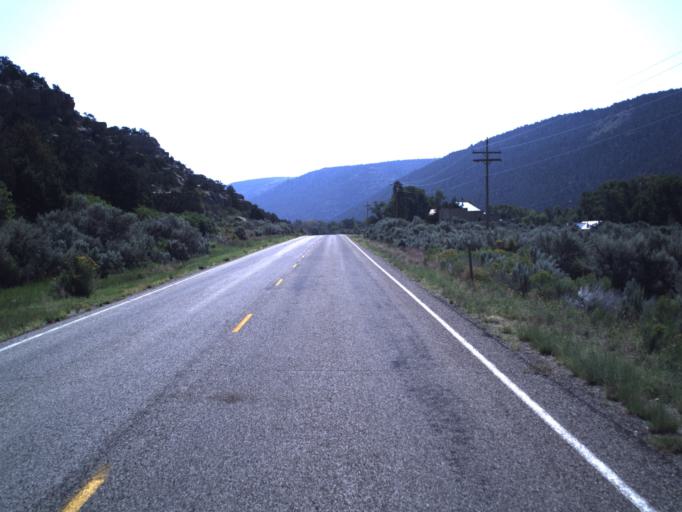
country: US
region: Utah
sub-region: Duchesne County
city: Duchesne
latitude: 40.3070
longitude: -110.6322
